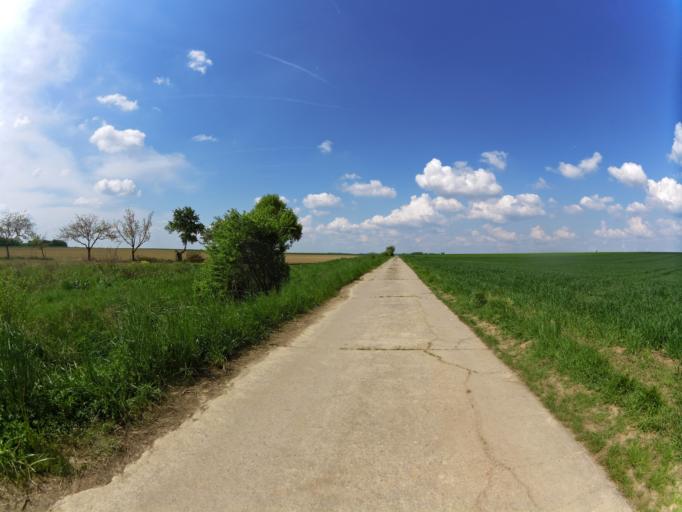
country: DE
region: Bavaria
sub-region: Regierungsbezirk Unterfranken
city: Giebelstadt
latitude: 49.6354
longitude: 9.9382
